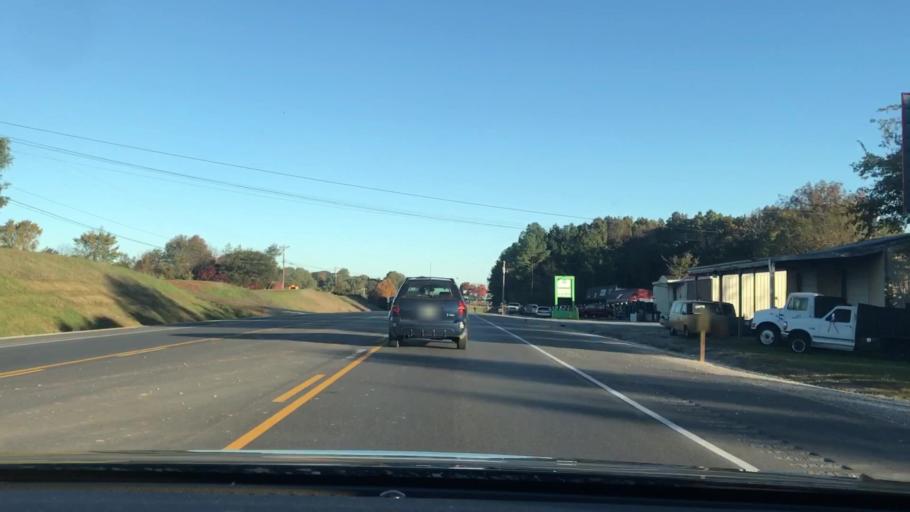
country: US
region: Kentucky
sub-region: Simpson County
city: Franklin
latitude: 36.6829
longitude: -86.5670
